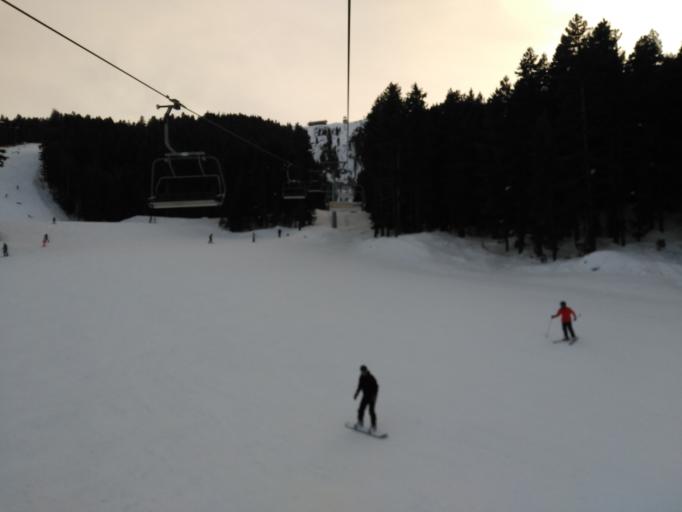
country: BG
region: Blagoevgrad
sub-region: Obshtina Bansko
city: Bansko
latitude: 41.7705
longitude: 23.4484
